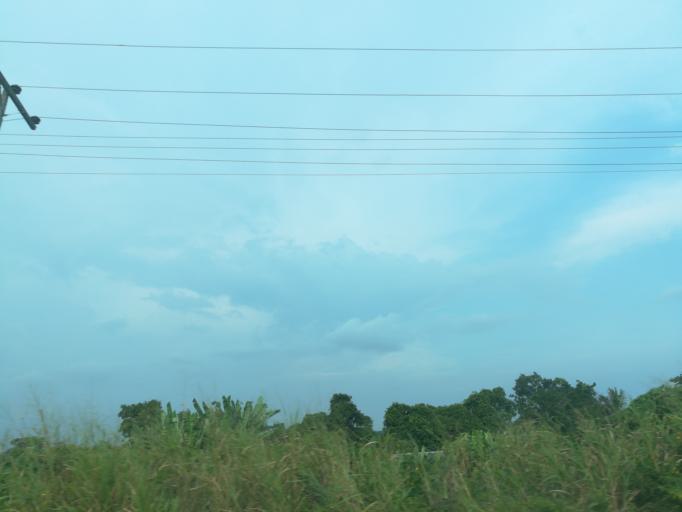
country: NG
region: Lagos
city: Ikorodu
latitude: 6.6494
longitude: 3.6695
